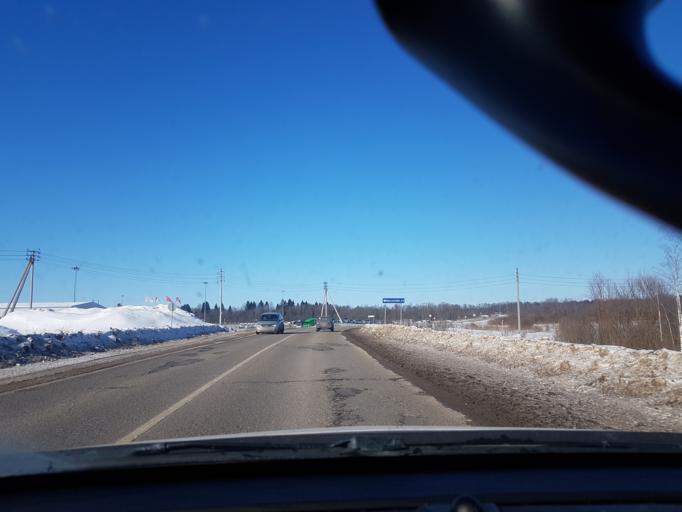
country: RU
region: Moskovskaya
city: Sychevo
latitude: 55.9991
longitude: 36.2346
